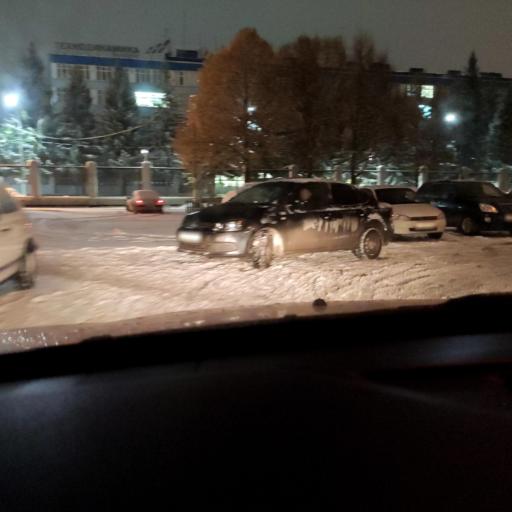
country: RU
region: Samara
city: Smyshlyayevka
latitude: 53.2117
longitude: 50.2902
